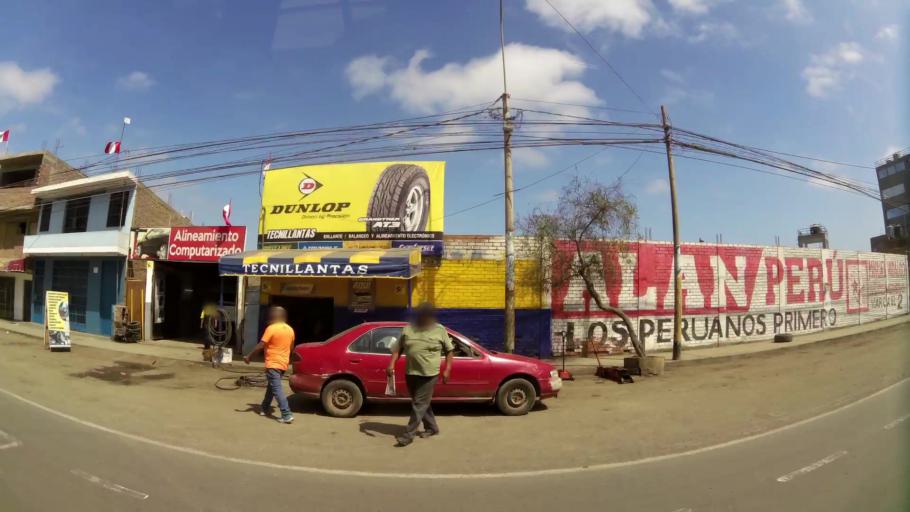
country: PE
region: Lima
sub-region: Provincia de Canete
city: Mala
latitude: -12.6589
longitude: -76.6344
